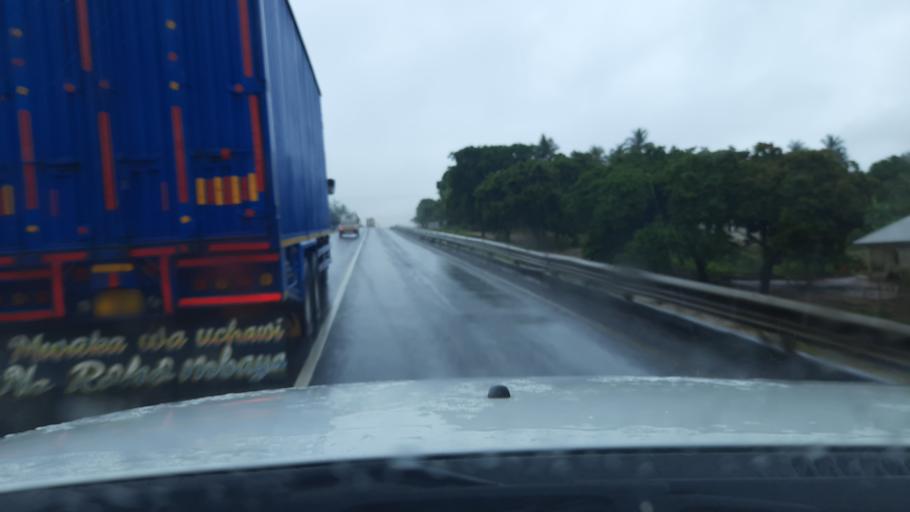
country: TZ
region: Pwani
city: Bagamoyo
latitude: -6.5866
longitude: 39.0501
